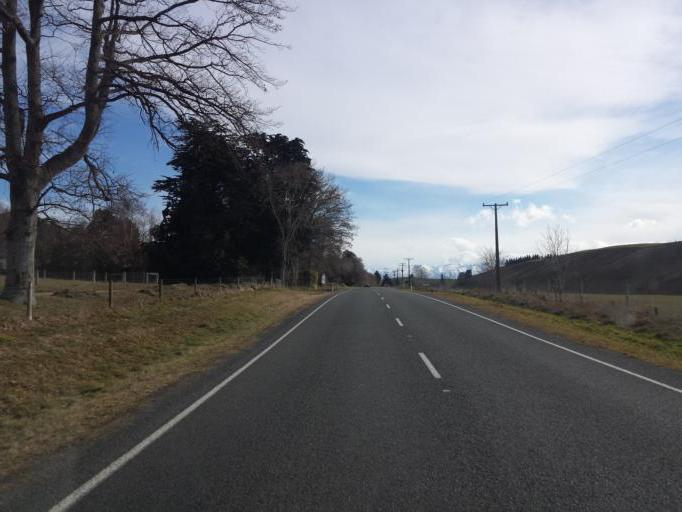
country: NZ
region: Canterbury
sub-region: Timaru District
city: Pleasant Point
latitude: -44.1145
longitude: 171.0182
